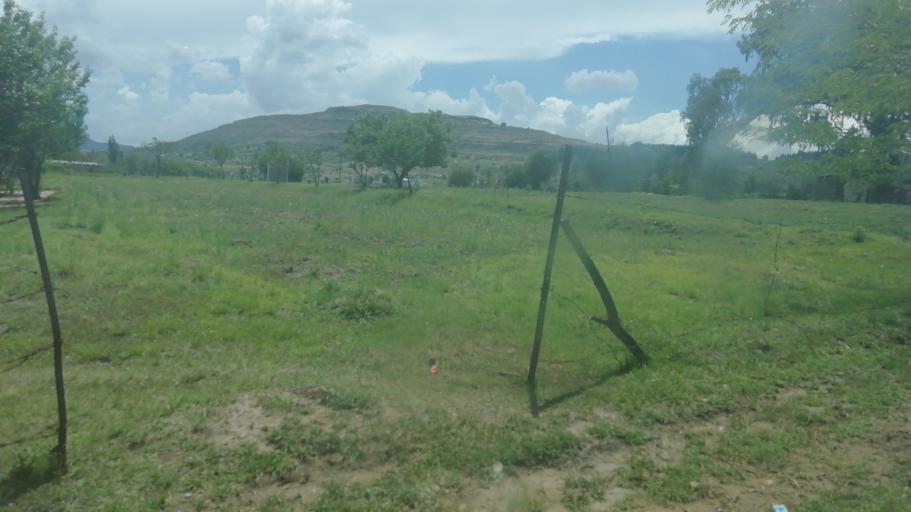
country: LS
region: Maseru
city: Nako
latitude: -29.6203
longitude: 27.5097
